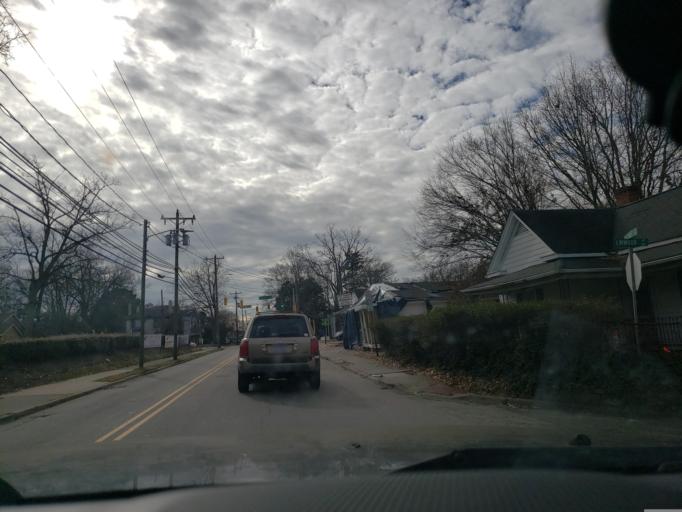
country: US
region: North Carolina
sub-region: Durham County
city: Durham
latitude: 35.9813
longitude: -78.8993
